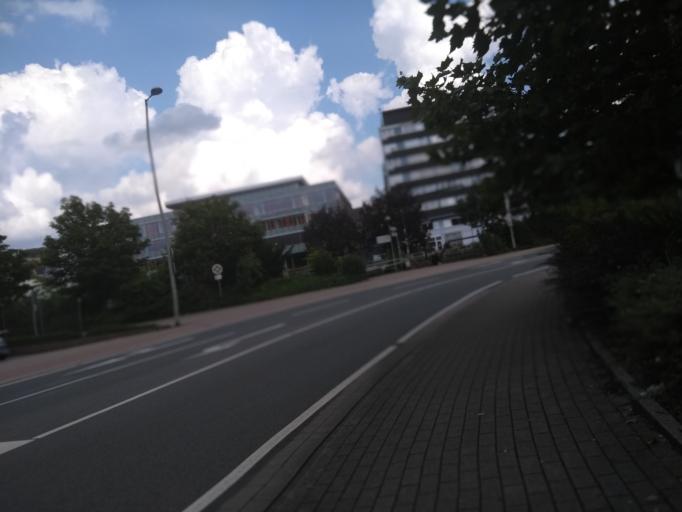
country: DE
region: North Rhine-Westphalia
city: Wetter (Ruhr)
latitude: 51.3854
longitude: 7.3862
